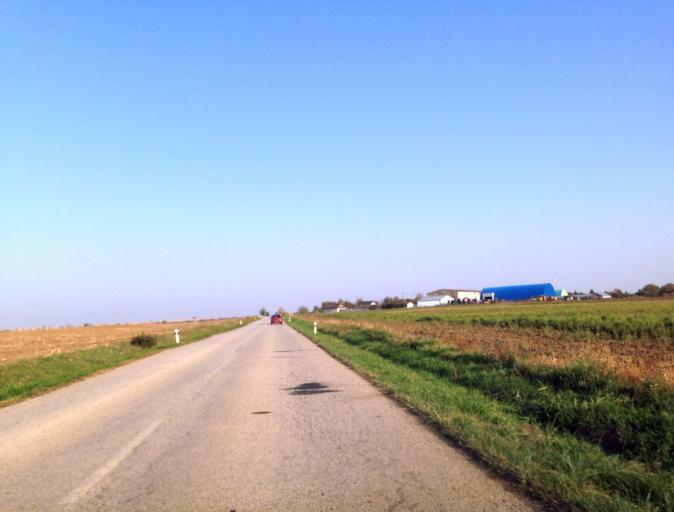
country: SK
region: Nitriansky
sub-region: Okres Komarno
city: Hurbanovo
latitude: 47.8932
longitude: 18.2395
